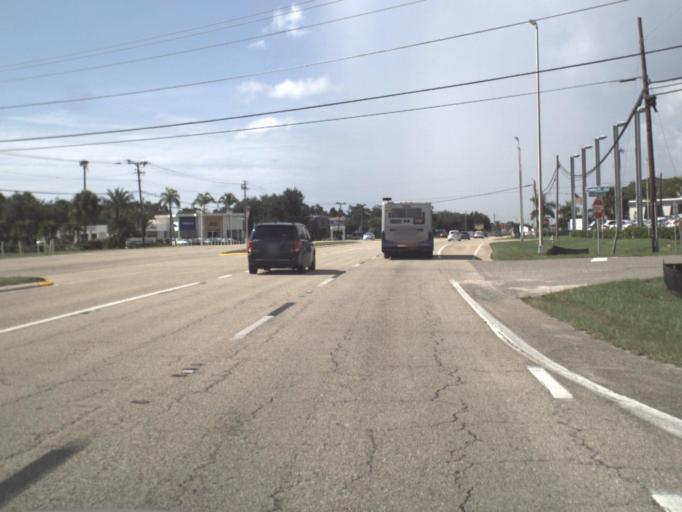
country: US
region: Florida
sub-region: Sarasota County
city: Gulf Gate Estates
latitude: 27.2431
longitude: -82.5089
